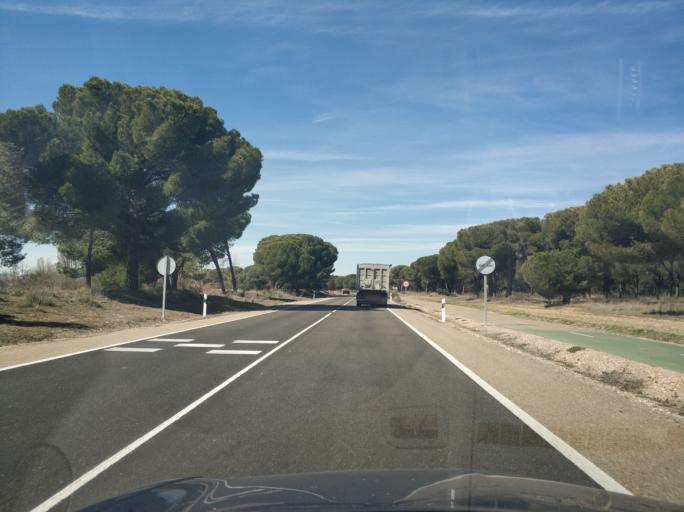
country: ES
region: Castille and Leon
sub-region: Provincia de Valladolid
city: Simancas
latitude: 41.5630
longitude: -4.7906
